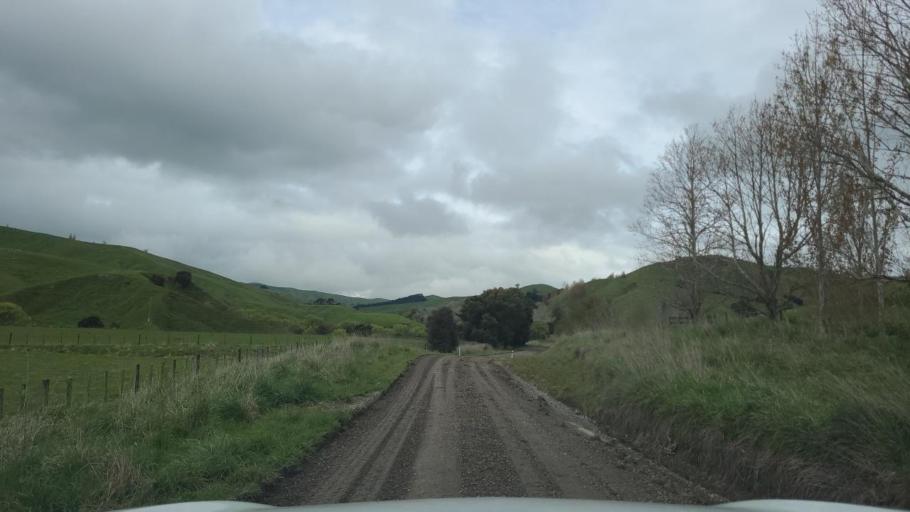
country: NZ
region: Wellington
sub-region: South Wairarapa District
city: Waipawa
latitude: -41.1936
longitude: 175.5933
